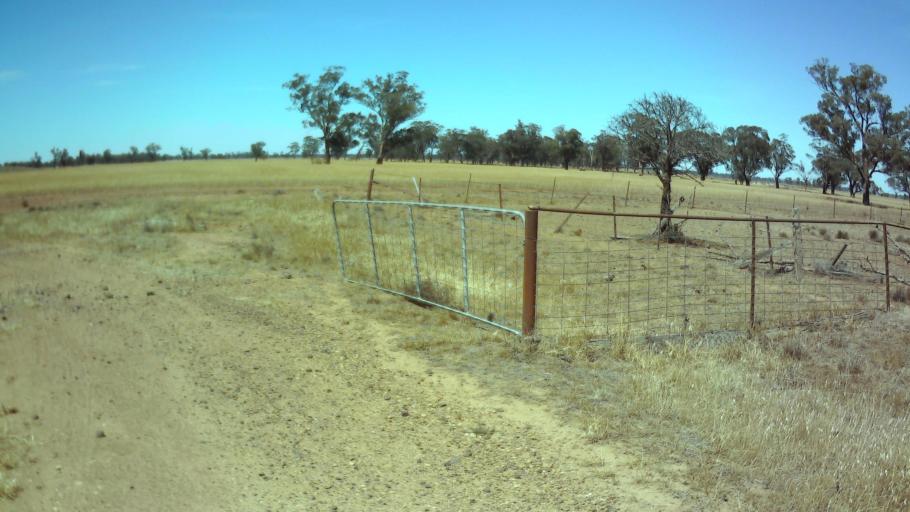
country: AU
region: New South Wales
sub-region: Weddin
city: Grenfell
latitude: -34.0661
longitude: 147.8760
